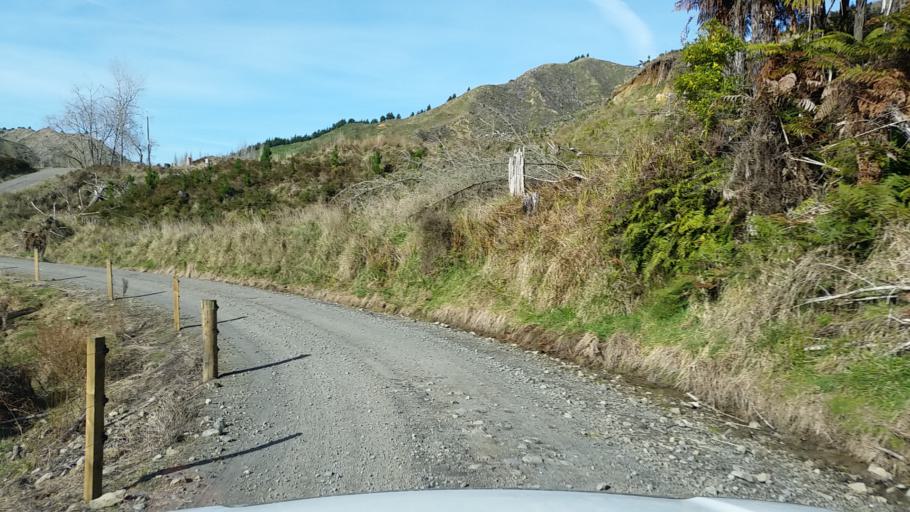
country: NZ
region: Taranaki
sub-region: South Taranaki District
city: Eltham
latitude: -39.3630
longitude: 174.5152
